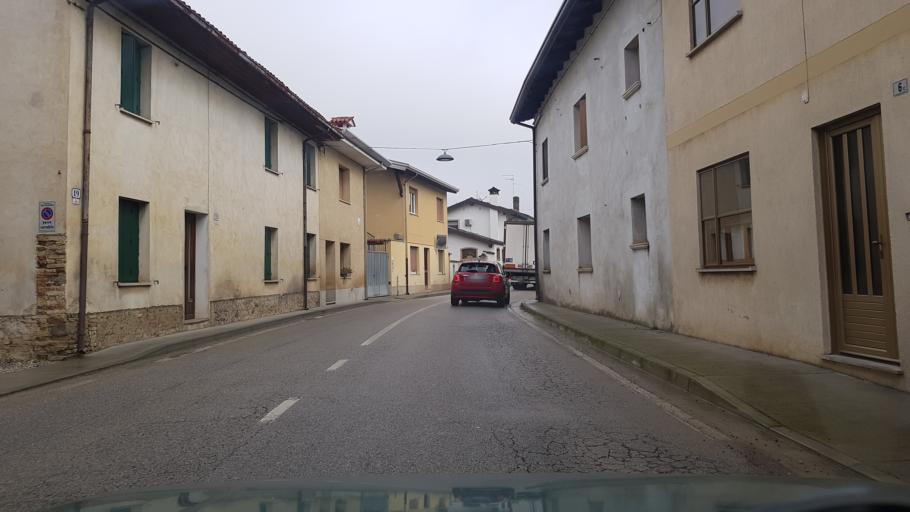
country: IT
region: Friuli Venezia Giulia
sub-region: Provincia di Udine
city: Ialmicco
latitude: 45.9136
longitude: 13.3465
